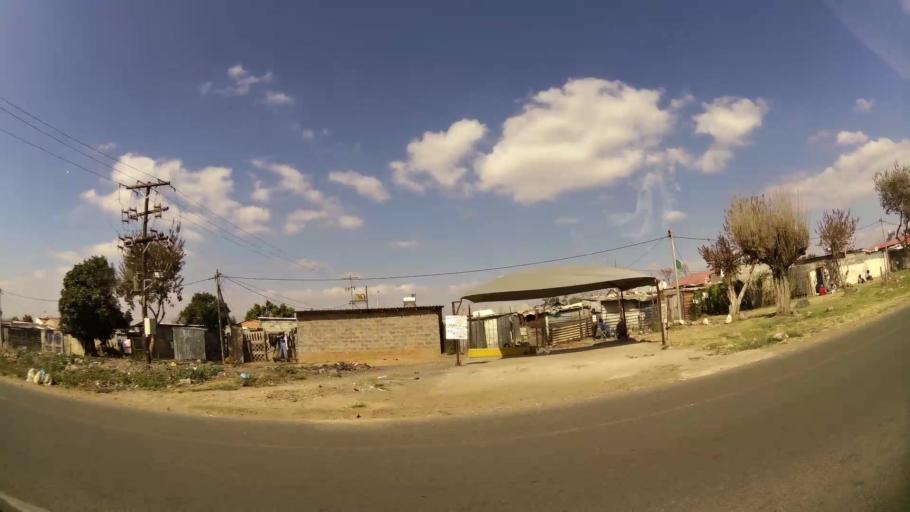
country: ZA
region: Gauteng
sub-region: City of Johannesburg Metropolitan Municipality
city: Midrand
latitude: -26.0071
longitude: 28.1738
